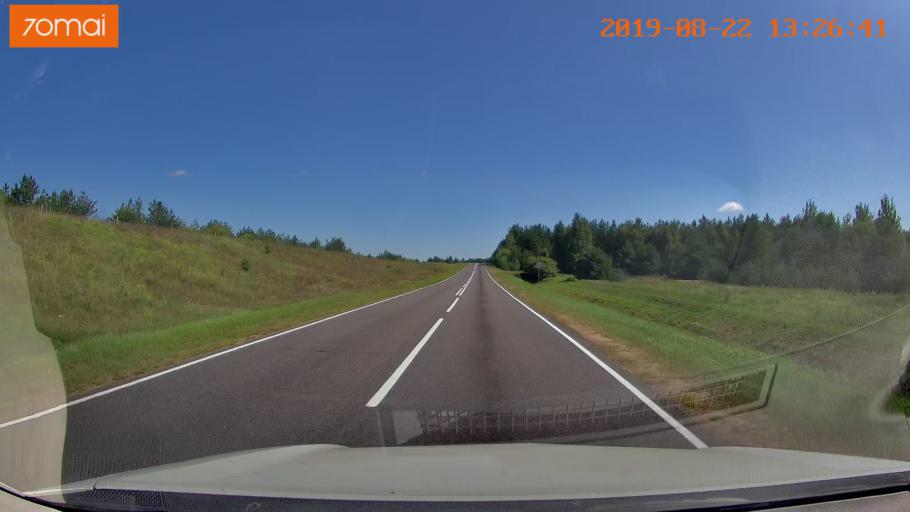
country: BY
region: Minsk
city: Staryya Darohi
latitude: 53.2084
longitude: 28.0679
